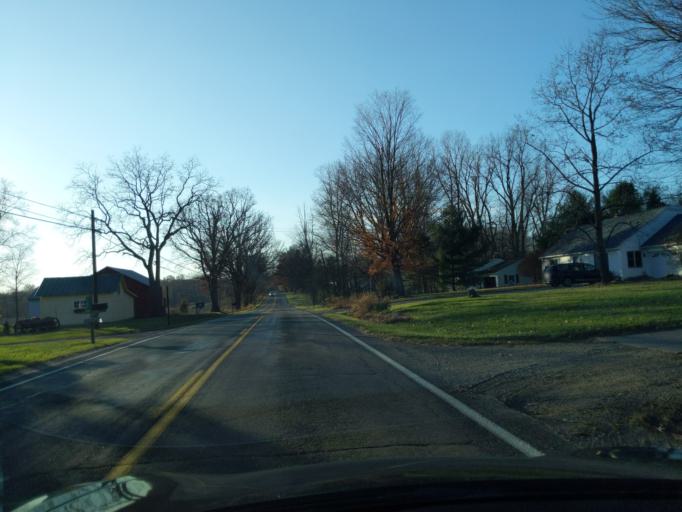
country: US
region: Michigan
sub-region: Ingham County
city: Williamston
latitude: 42.7155
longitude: -84.3354
